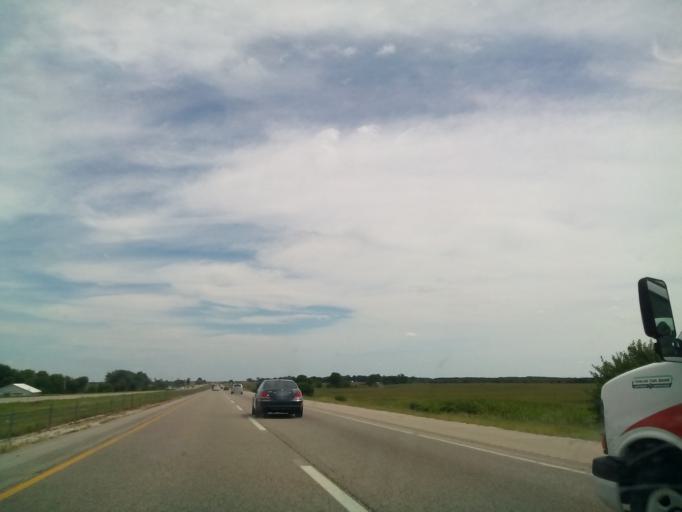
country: US
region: Illinois
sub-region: Kane County
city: Maple Park
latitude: 41.8708
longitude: -88.5906
